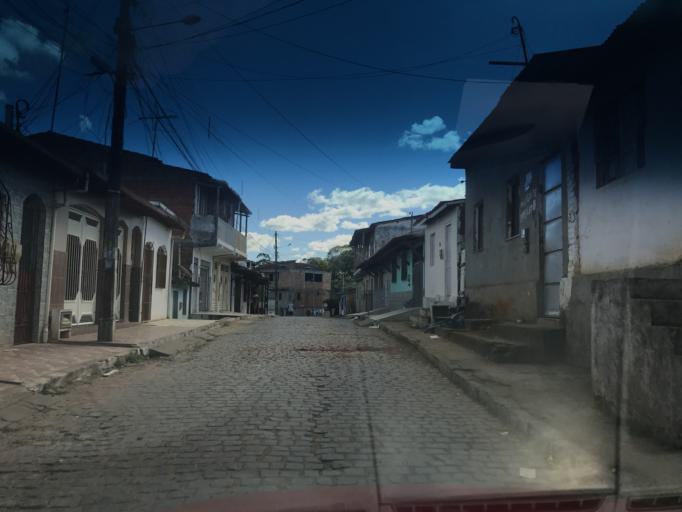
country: BR
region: Bahia
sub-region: Gandu
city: Gandu
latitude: -13.7455
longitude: -39.4928
